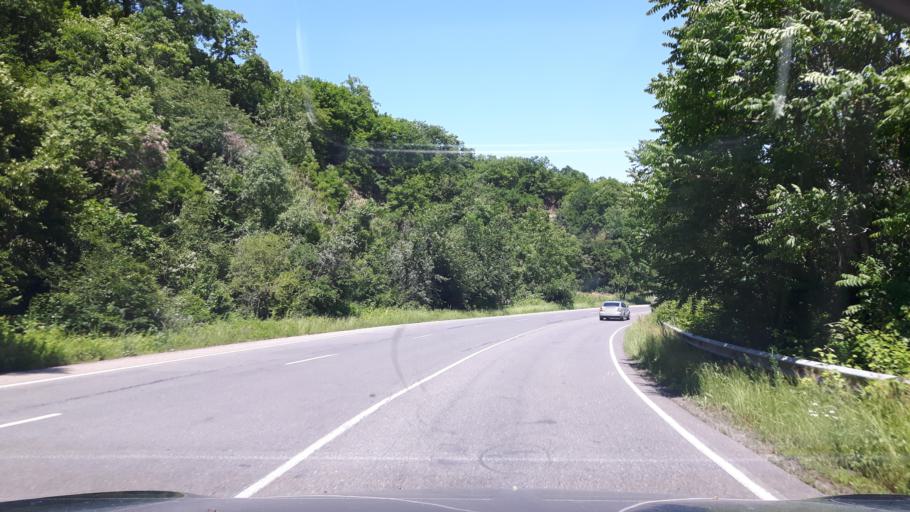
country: GE
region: Kakheti
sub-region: Gurjaani
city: Gurjaani
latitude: 41.6757
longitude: 45.8375
